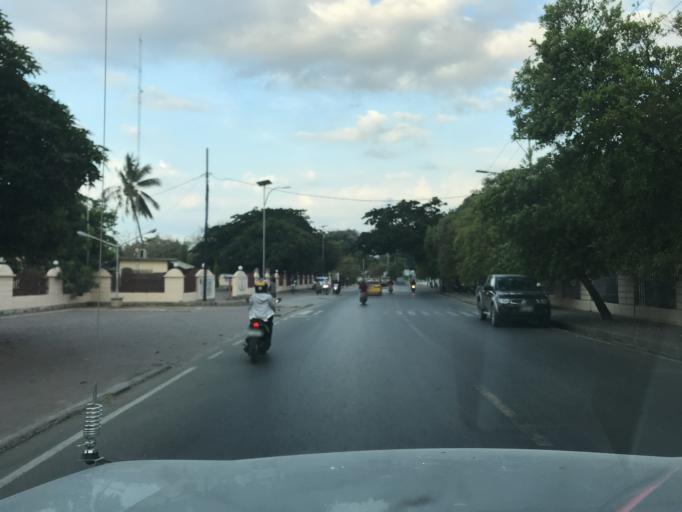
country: TL
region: Dili
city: Dili
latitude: -8.5522
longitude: 125.5812
